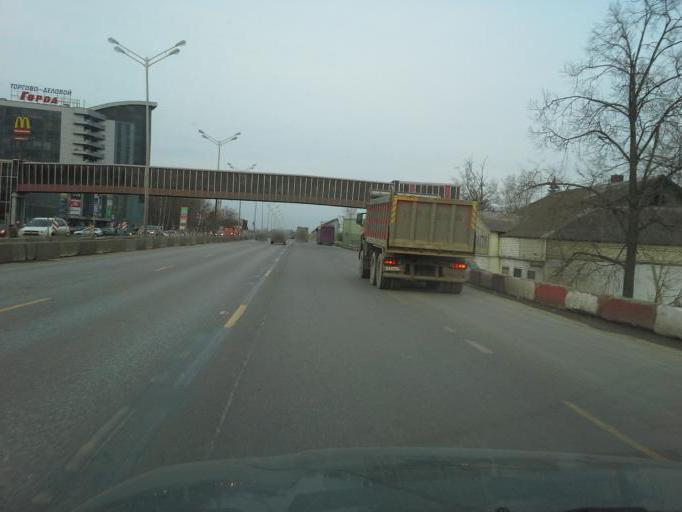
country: RU
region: Moskovskaya
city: Lesnoy Gorodok
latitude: 55.6311
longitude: 37.2102
